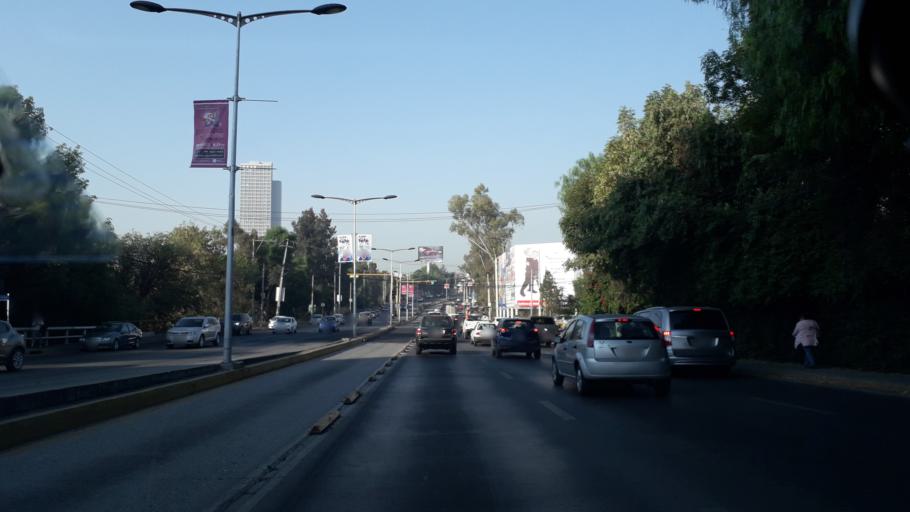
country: MX
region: Puebla
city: Puebla
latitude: 19.0425
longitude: -98.2373
